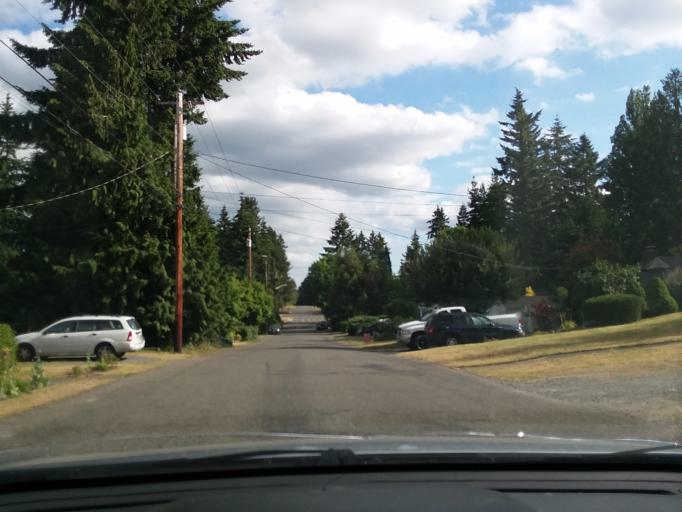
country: US
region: Washington
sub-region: Snohomish County
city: Mountlake Terrace
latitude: 47.7862
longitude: -122.3030
